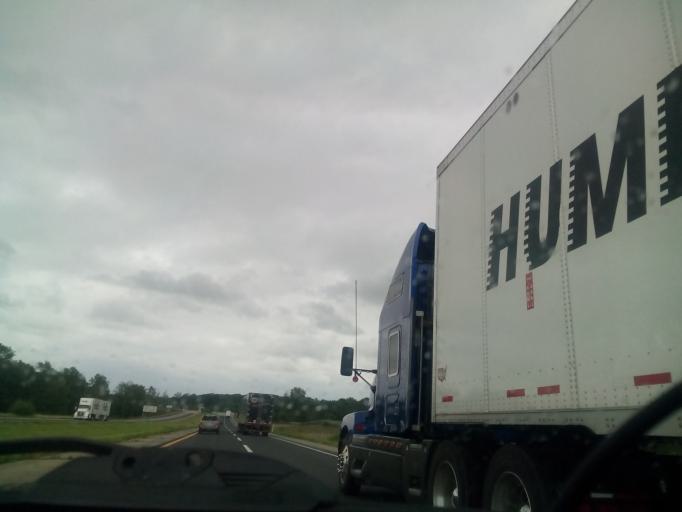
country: US
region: Indiana
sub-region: Steuben County
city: Hamilton
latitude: 41.6341
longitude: -84.8227
